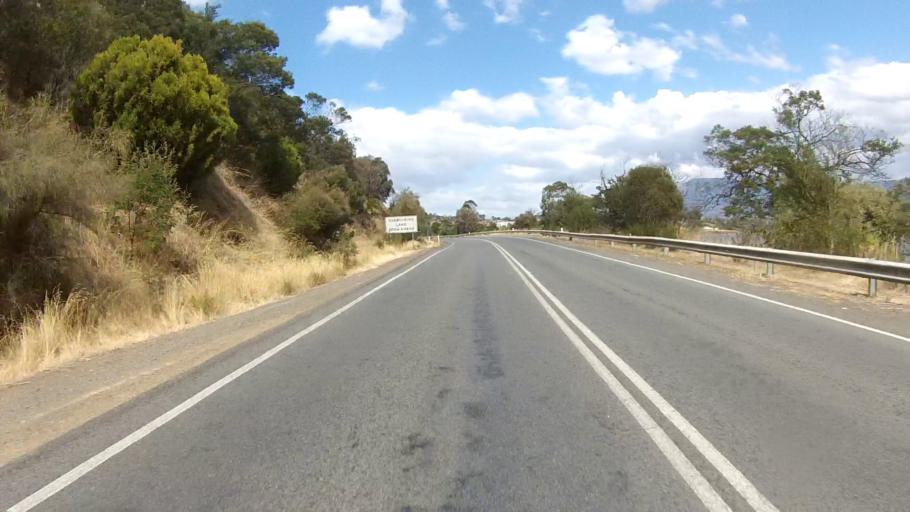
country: AU
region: Tasmania
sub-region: Brighton
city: Old Beach
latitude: -42.7865
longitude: 147.2912
